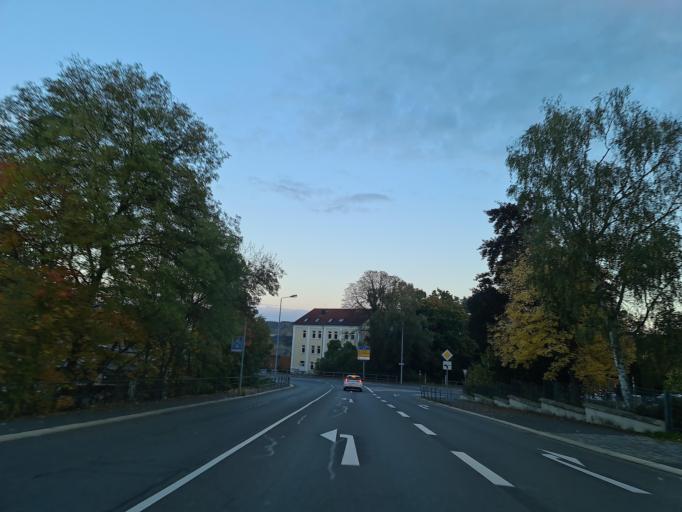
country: DE
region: Saxony
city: Plauen
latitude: 50.4907
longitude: 12.1251
